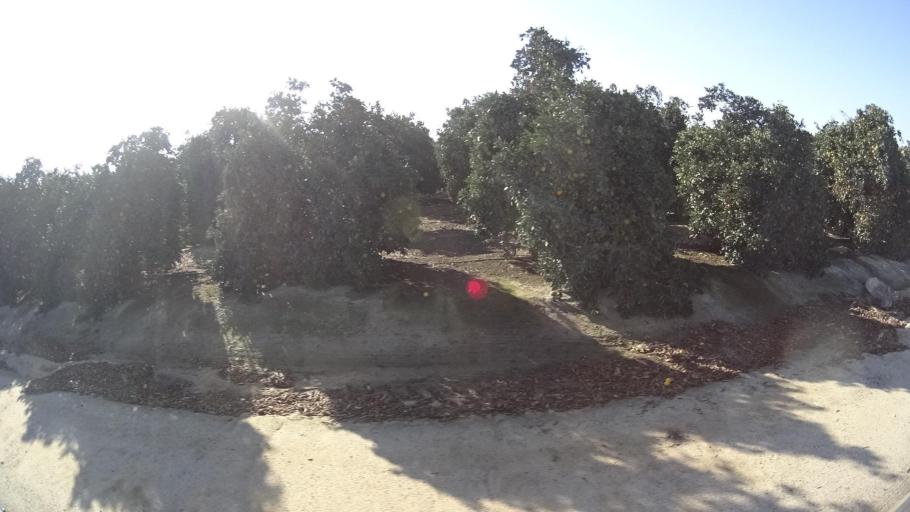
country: US
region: California
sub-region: Tulare County
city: Richgrove
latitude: 35.7253
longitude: -119.1464
